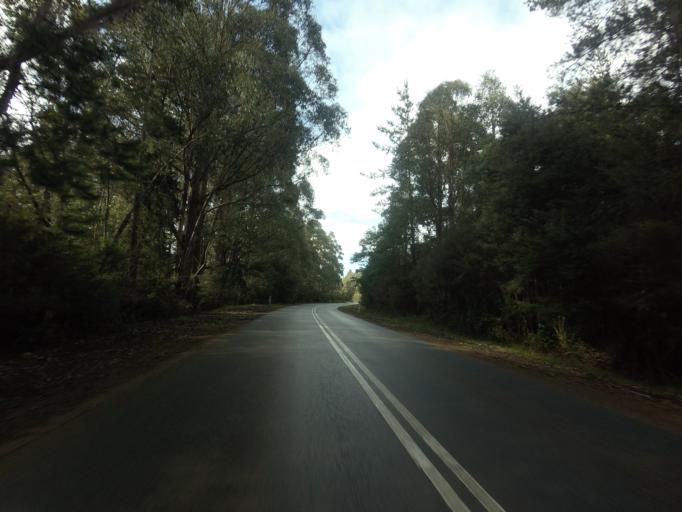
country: AU
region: Tasmania
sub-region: Huon Valley
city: Geeveston
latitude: -43.3531
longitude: 146.9572
